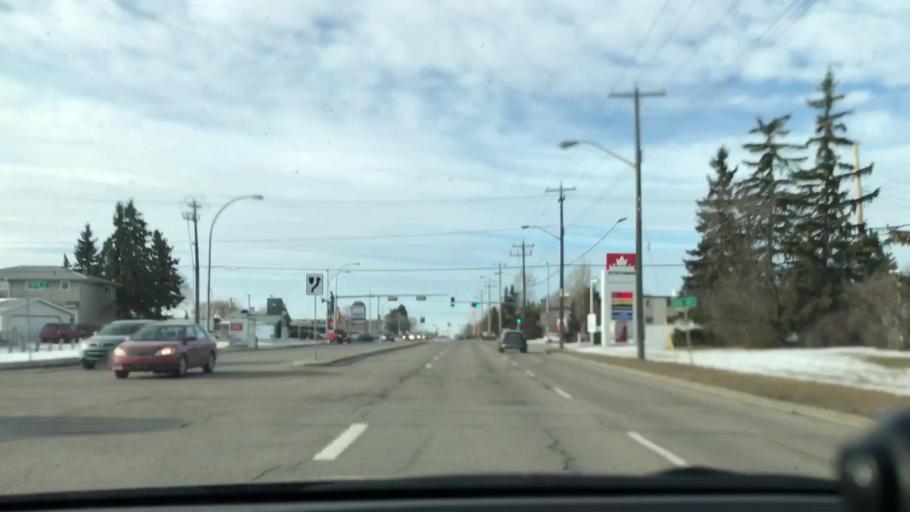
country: CA
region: Alberta
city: Edmonton
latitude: 53.4883
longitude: -113.5026
